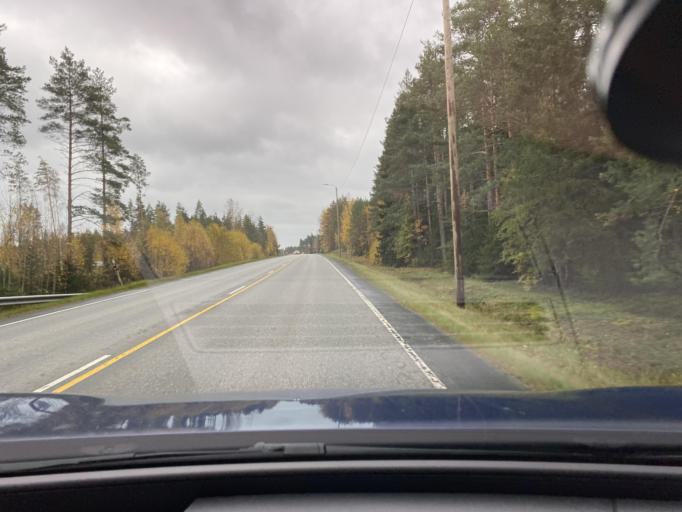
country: FI
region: Varsinais-Suomi
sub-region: Vakka-Suomi
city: Laitila
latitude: 60.9619
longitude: 21.5947
